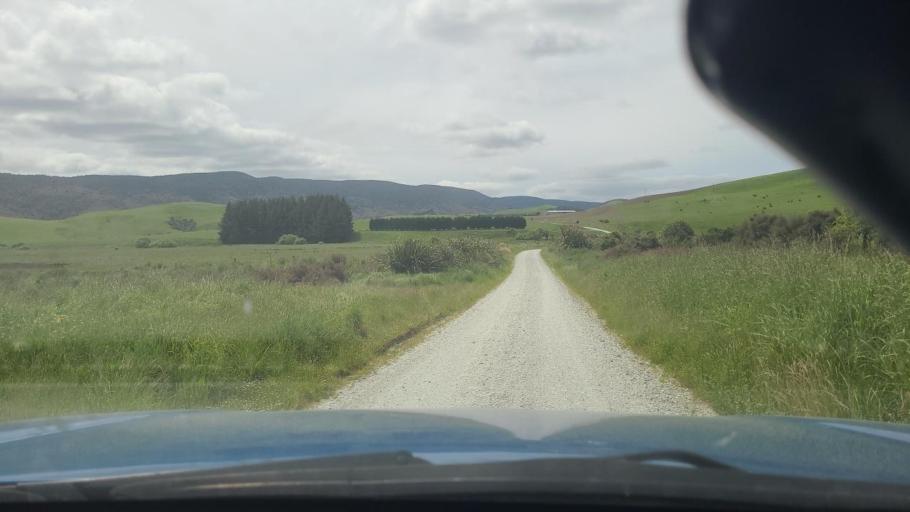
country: NZ
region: Otago
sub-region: Clutha District
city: Papatowai
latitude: -46.5113
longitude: 169.1477
